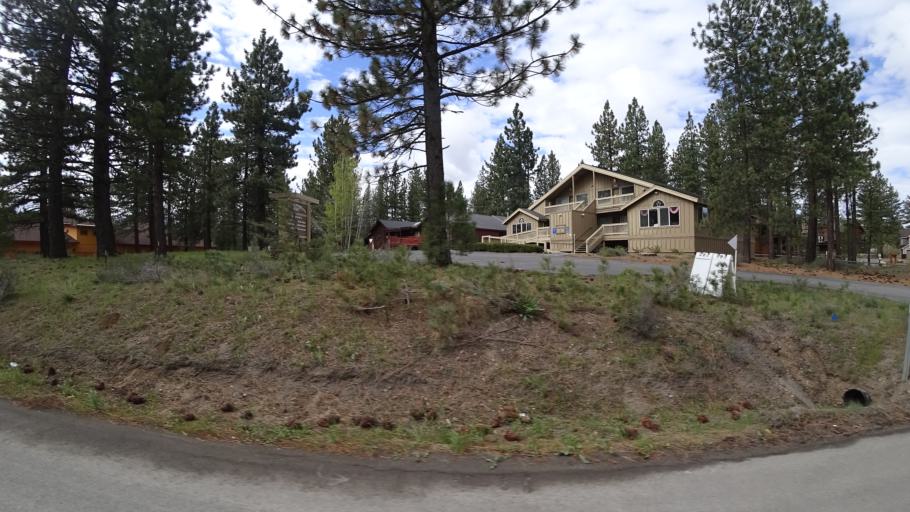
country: US
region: California
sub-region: Nevada County
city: Truckee
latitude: 39.3164
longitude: -120.1527
